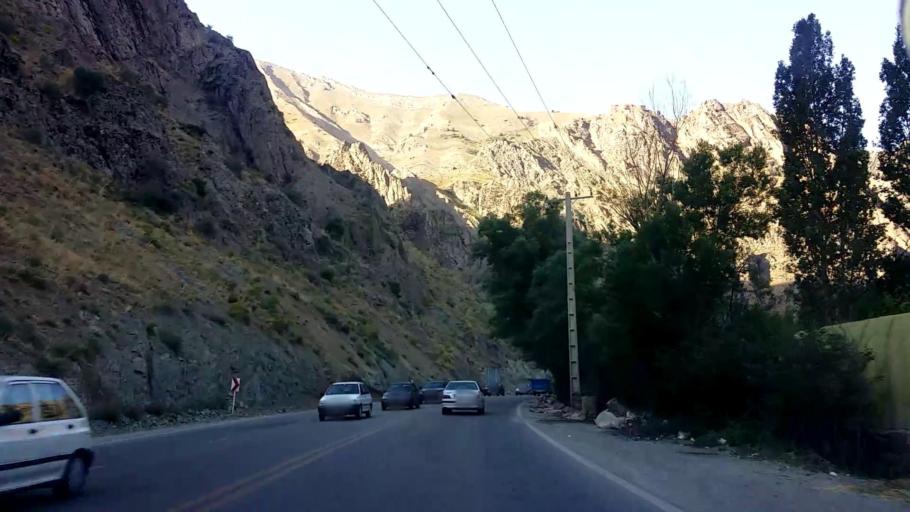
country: IR
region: Tehran
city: Tajrish
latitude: 36.0297
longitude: 51.3135
